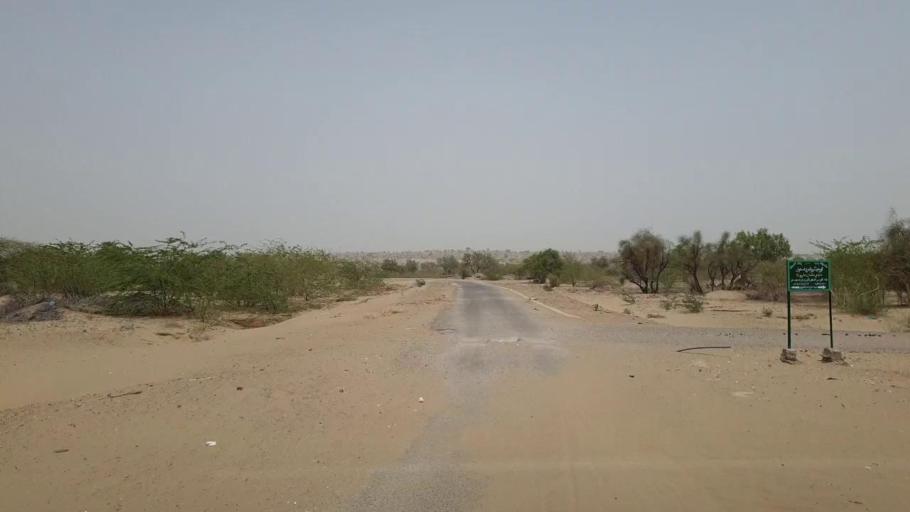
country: PK
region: Sindh
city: Islamkot
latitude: 24.7968
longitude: 70.5411
